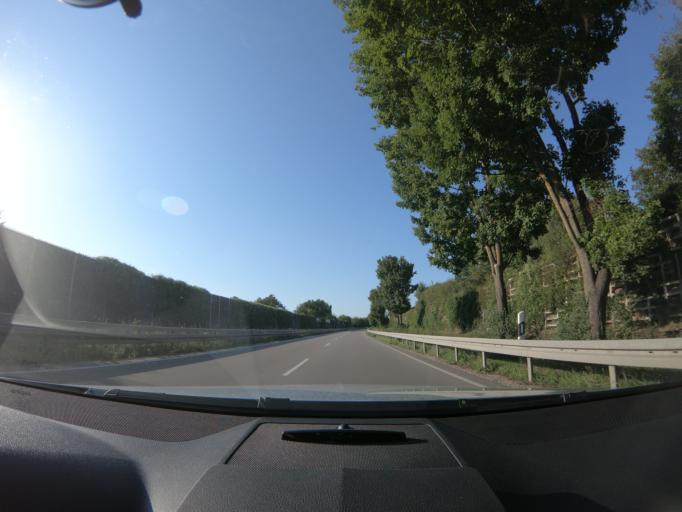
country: DE
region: Bavaria
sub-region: Upper Bavaria
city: Unterschleissheim
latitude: 48.2742
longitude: 11.5908
